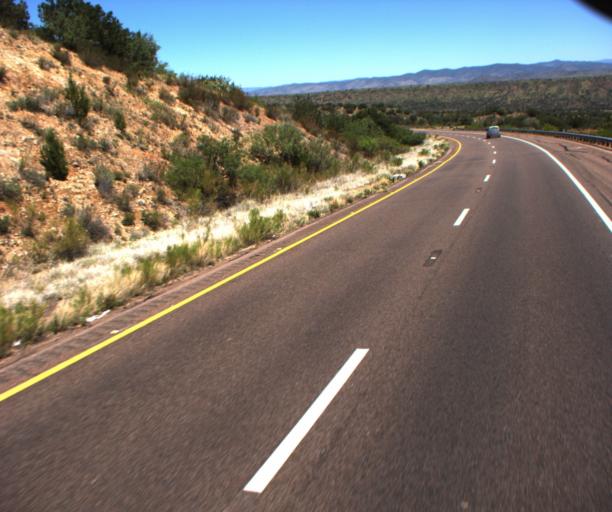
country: US
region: Arizona
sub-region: Gila County
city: Tonto Basin
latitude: 34.0158
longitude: -111.3587
